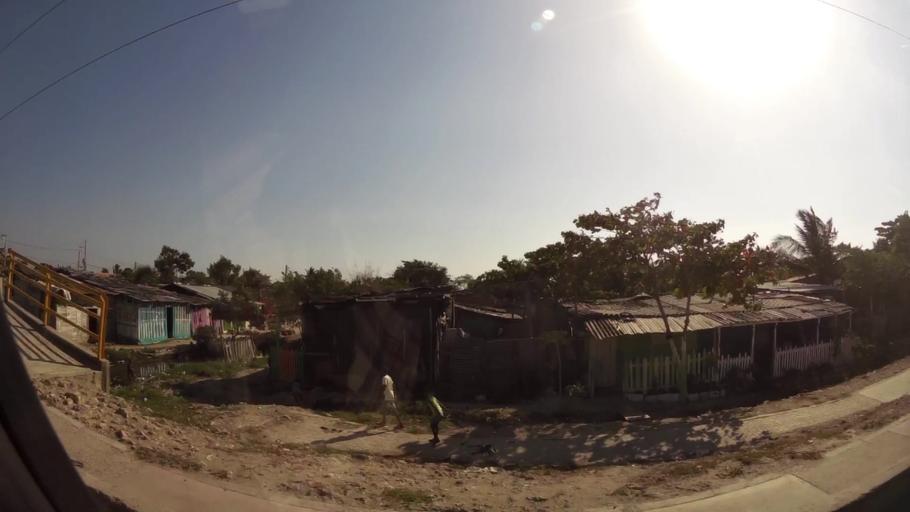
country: CO
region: Bolivar
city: Cartagena
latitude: 10.4158
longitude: -75.5116
